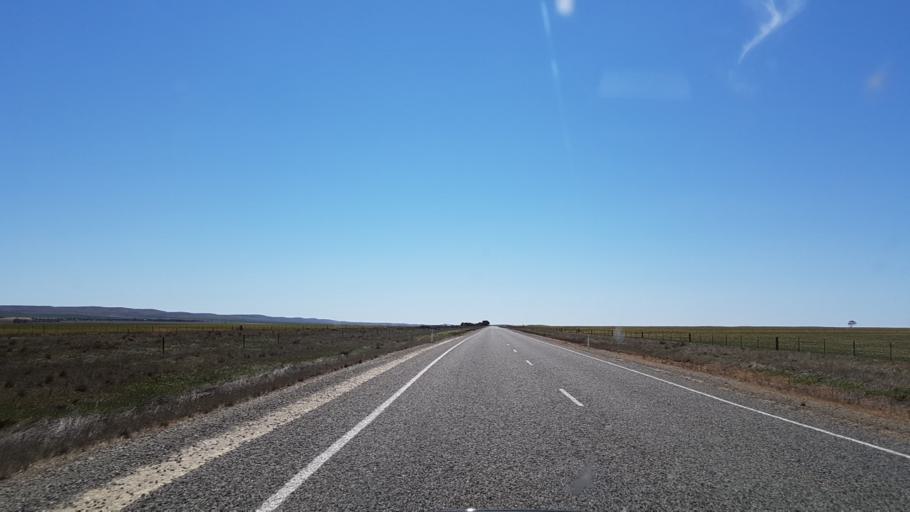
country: AU
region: South Australia
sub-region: Northern Areas
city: Jamestown
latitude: -33.2667
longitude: 138.8686
